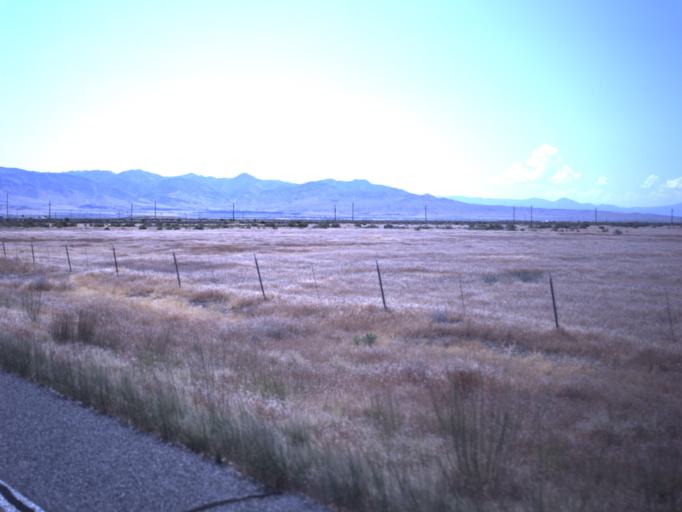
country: US
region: Utah
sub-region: Millard County
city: Delta
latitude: 39.4662
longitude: -112.4412
